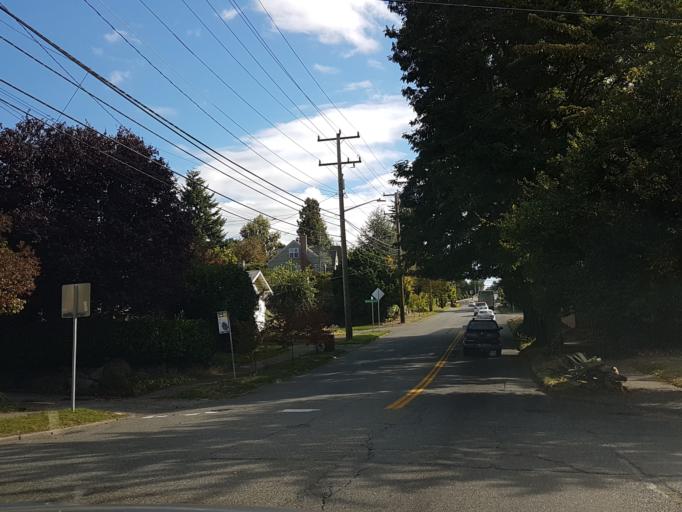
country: US
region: Washington
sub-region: King County
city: Shoreline
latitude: 47.6869
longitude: -122.3306
